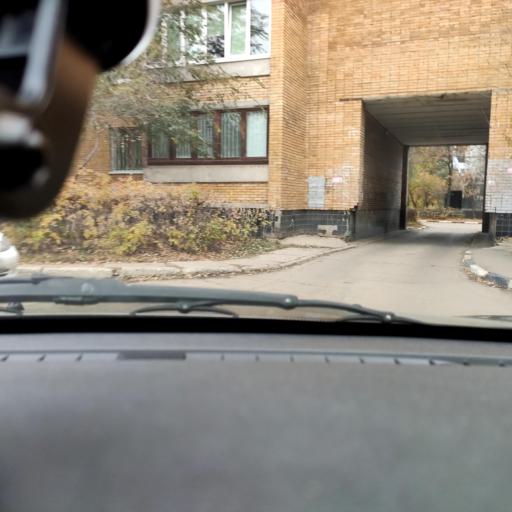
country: RU
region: Samara
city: Tol'yatti
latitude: 53.5192
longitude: 49.3089
